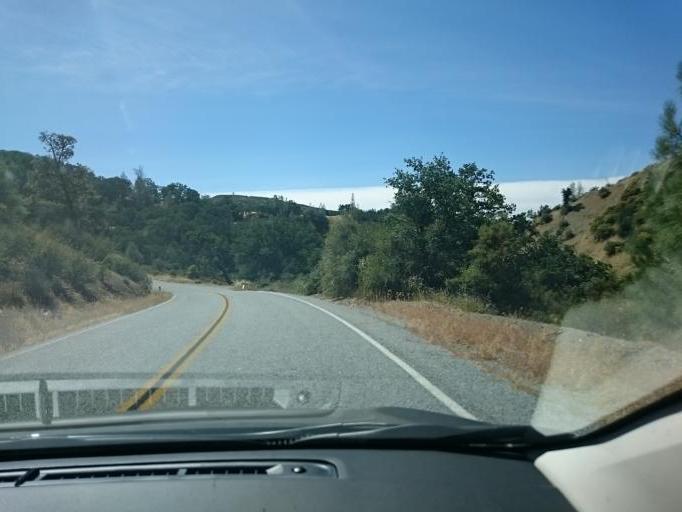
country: US
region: California
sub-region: Santa Clara County
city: Morgan Hill
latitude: 37.3579
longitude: -121.5707
